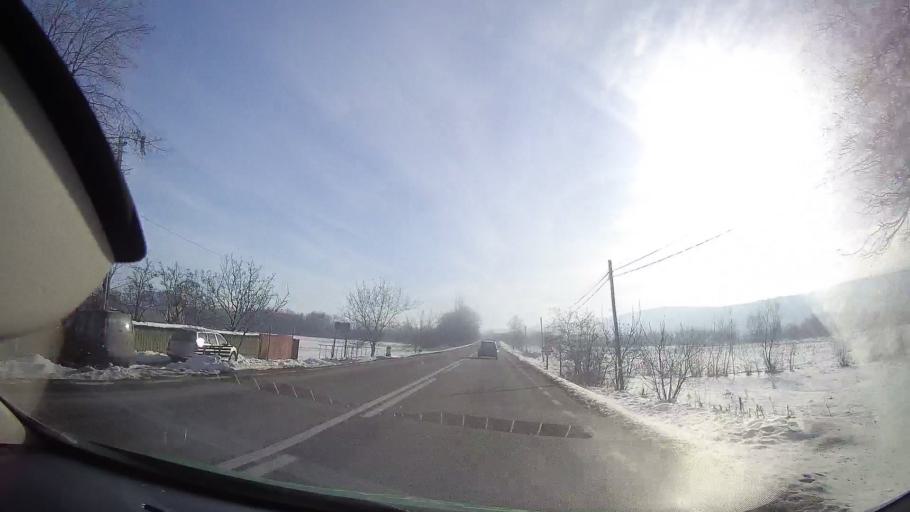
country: RO
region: Neamt
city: Bodesti
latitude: 47.0502
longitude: 26.4032
